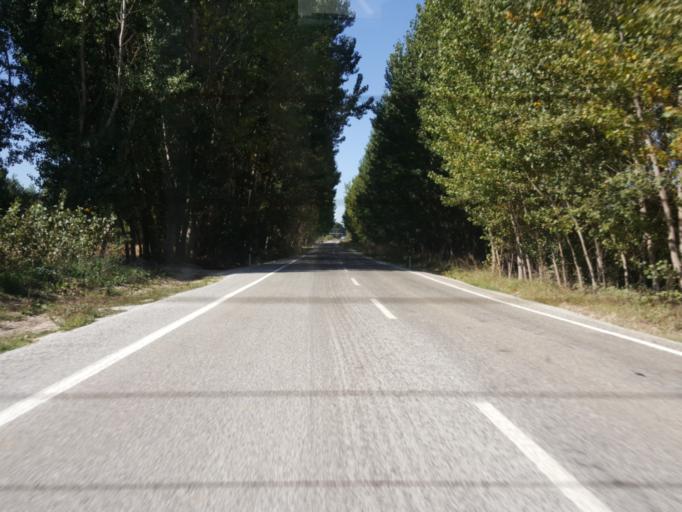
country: TR
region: Tokat
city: Pazar
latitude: 40.2682
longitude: 36.2080
